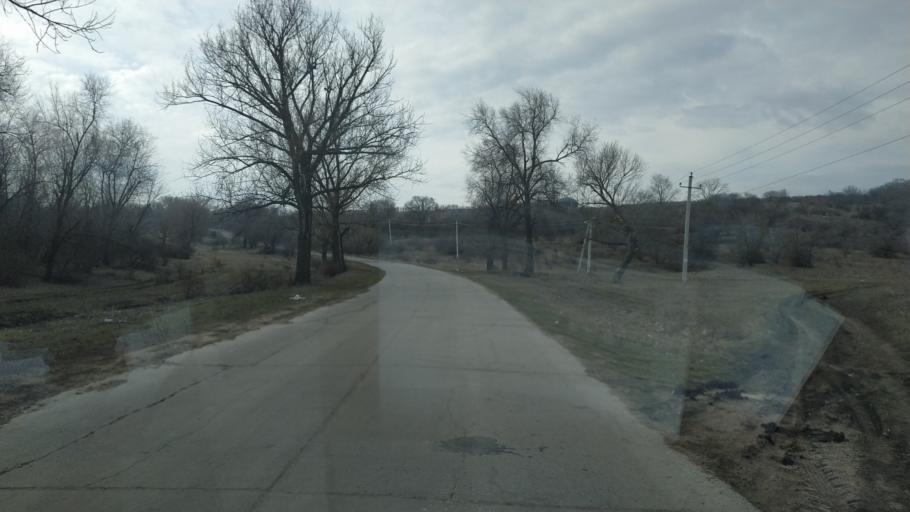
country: MD
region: Chisinau
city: Vadul lui Voda
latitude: 47.0055
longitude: 29.1129
